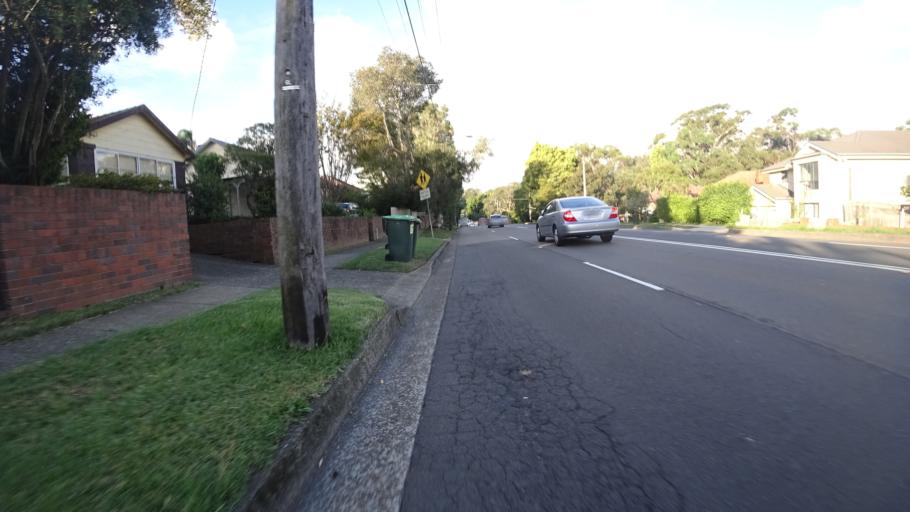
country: AU
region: New South Wales
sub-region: Lane Cove
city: Lane Cove West
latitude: -33.8176
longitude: 151.1582
